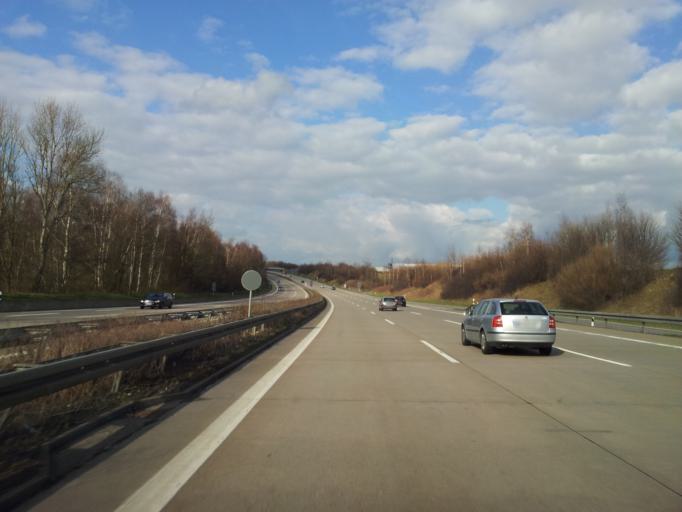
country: DE
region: Saxony
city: Frankenberg
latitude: 50.9293
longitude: 13.0547
